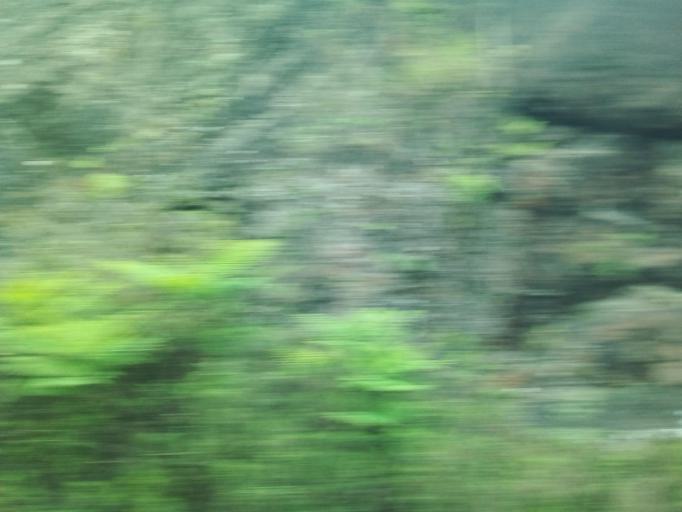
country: BR
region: Minas Gerais
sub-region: Joao Monlevade
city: Joao Monlevade
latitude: -19.8251
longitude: -43.1073
